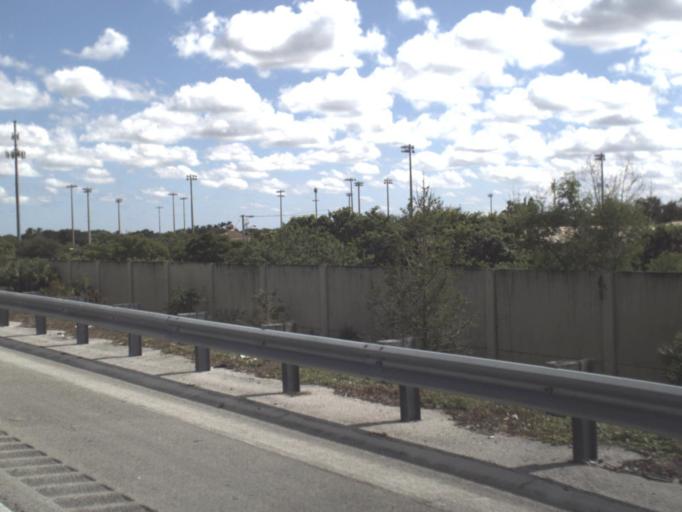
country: US
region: Florida
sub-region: Broward County
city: Coral Springs
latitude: 26.3019
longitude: -80.2680
